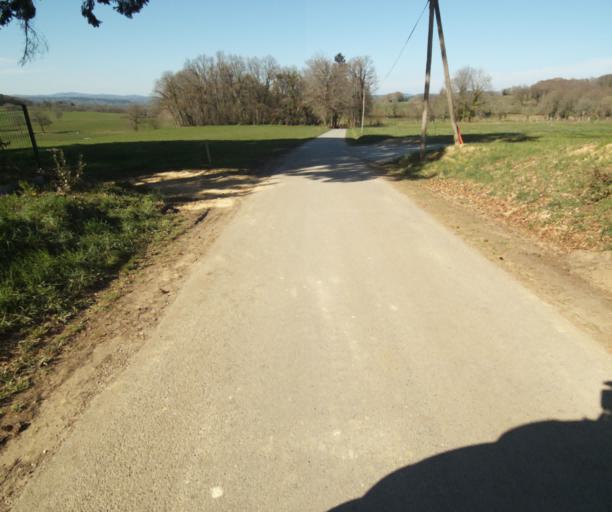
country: FR
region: Limousin
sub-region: Departement de la Correze
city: Chamboulive
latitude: 45.4725
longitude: 1.7358
